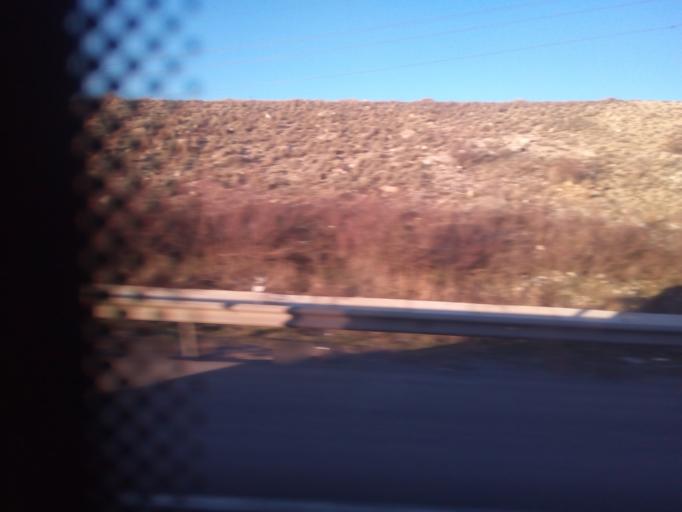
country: TR
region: Ankara
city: Etimesgut
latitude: 39.8791
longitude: 32.6276
